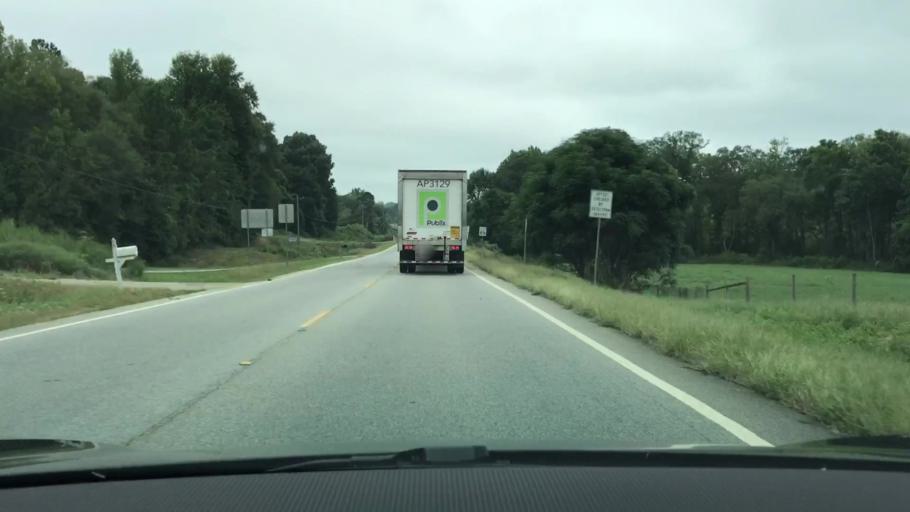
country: US
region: Georgia
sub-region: Oconee County
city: Watkinsville
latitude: 33.7301
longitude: -83.3027
